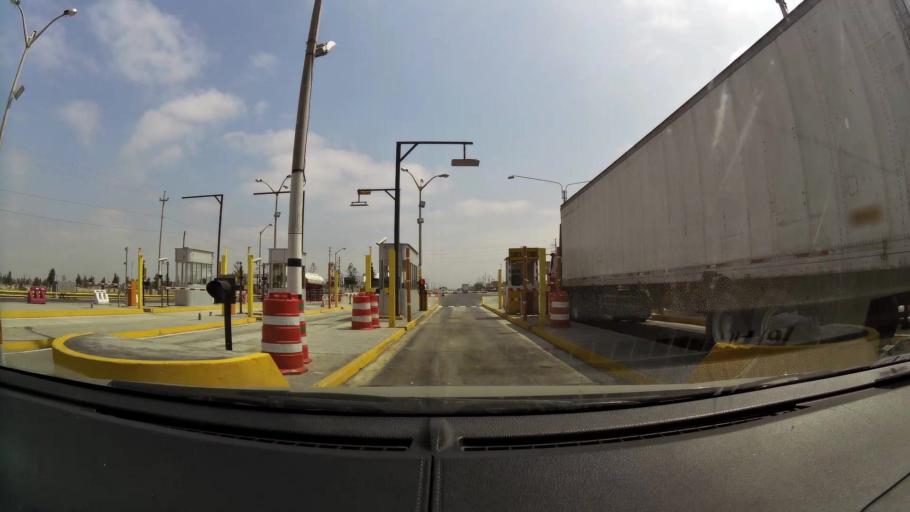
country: PE
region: La Libertad
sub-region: Ascope
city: Chicama
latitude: -7.8759
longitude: -79.1321
